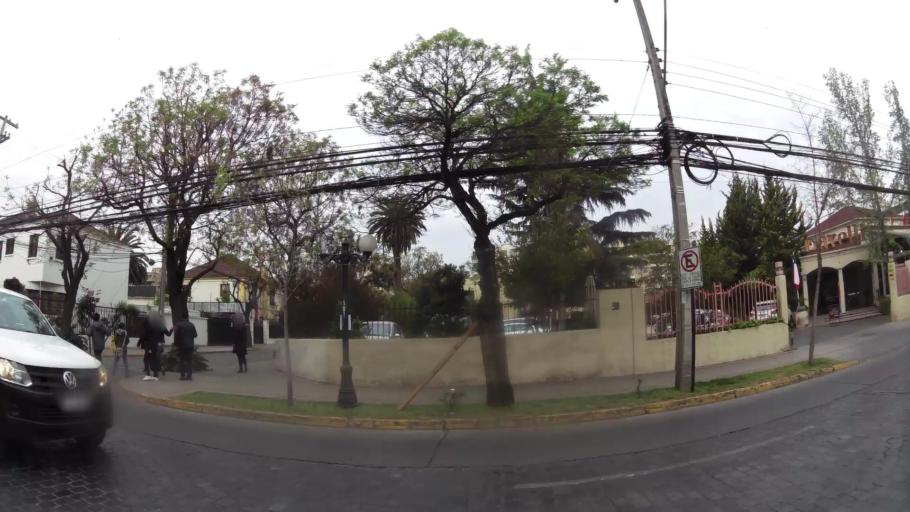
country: CL
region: Santiago Metropolitan
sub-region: Provincia de Santiago
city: Santiago
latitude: -33.4441
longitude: -70.6145
